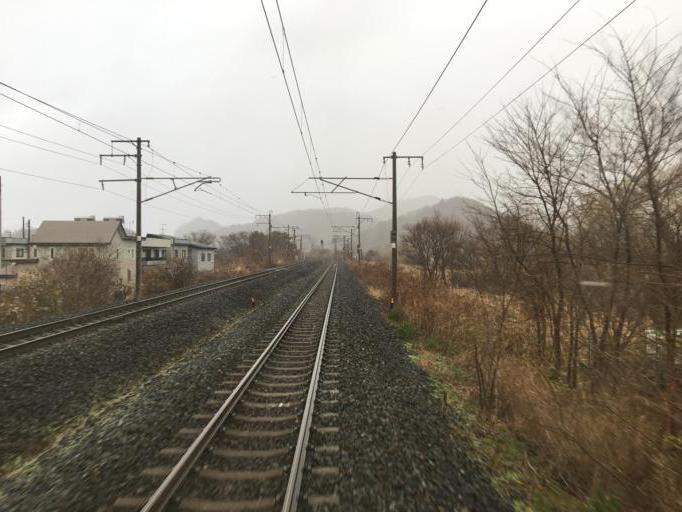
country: JP
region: Aomori
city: Aomori Shi
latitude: 40.8469
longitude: 140.8177
